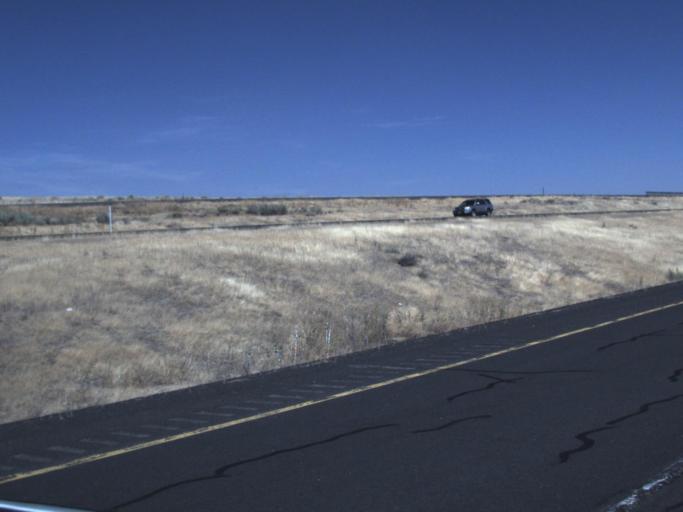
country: US
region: Washington
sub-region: Adams County
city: Ritzville
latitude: 47.0986
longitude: -118.6148
